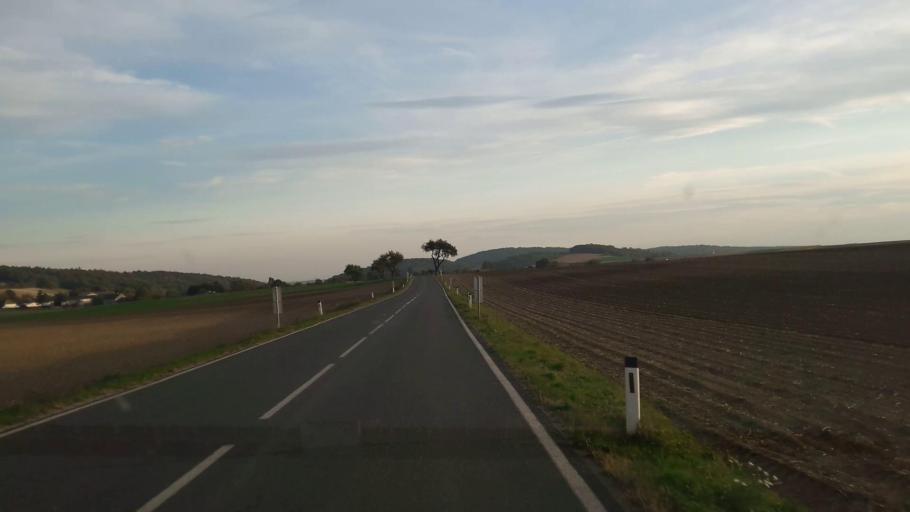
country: AT
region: Lower Austria
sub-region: Politischer Bezirk Korneuburg
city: Ernstbrunn
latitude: 48.5037
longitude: 16.3629
